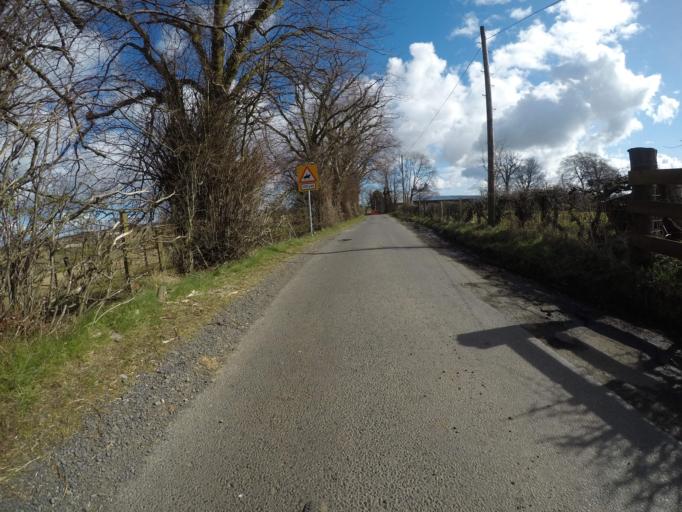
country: GB
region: Scotland
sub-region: North Ayrshire
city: Beith
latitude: 55.7209
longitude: -4.6178
